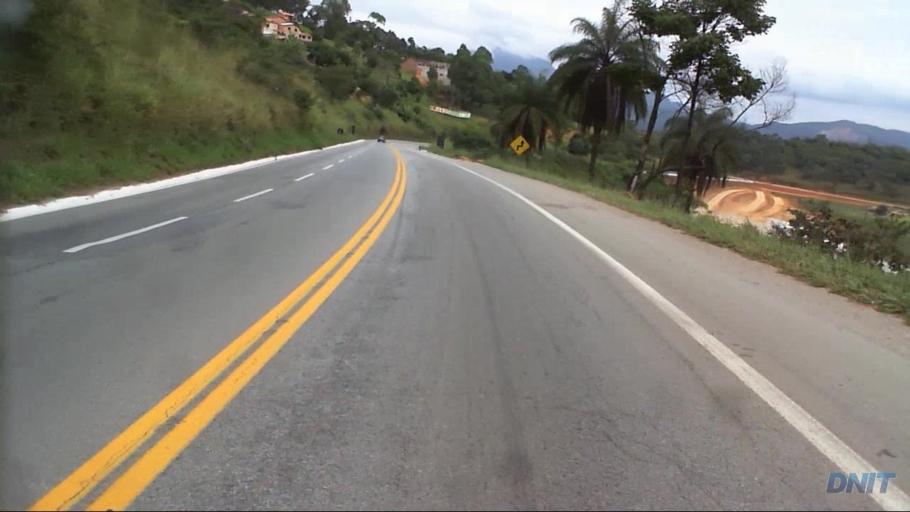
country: BR
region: Minas Gerais
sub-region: Caete
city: Caete
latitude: -19.7577
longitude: -43.6358
